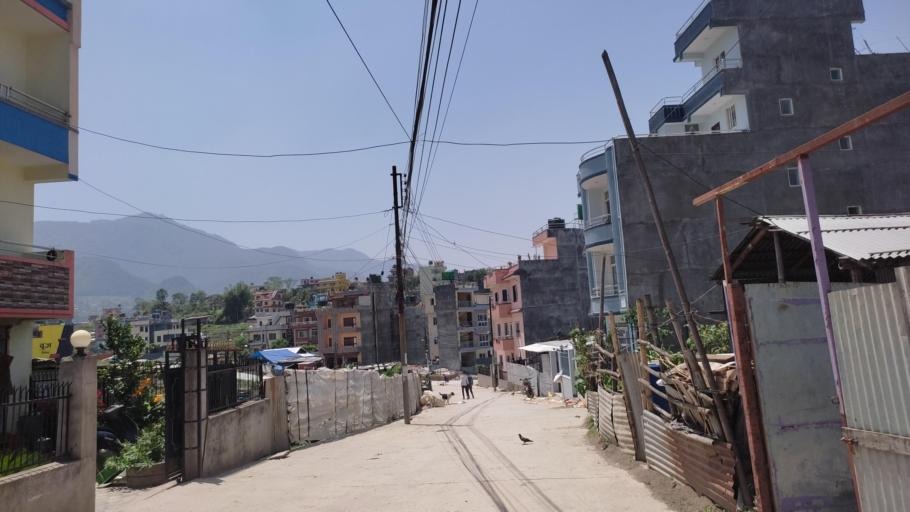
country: NP
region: Central Region
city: Kirtipur
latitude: 27.6740
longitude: 85.2701
